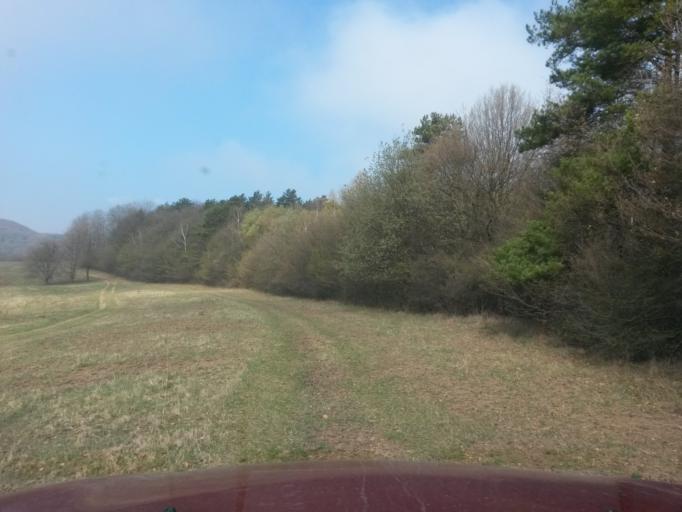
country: SK
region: Presovsky
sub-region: Okres Presov
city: Presov
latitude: 48.9219
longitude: 21.1710
